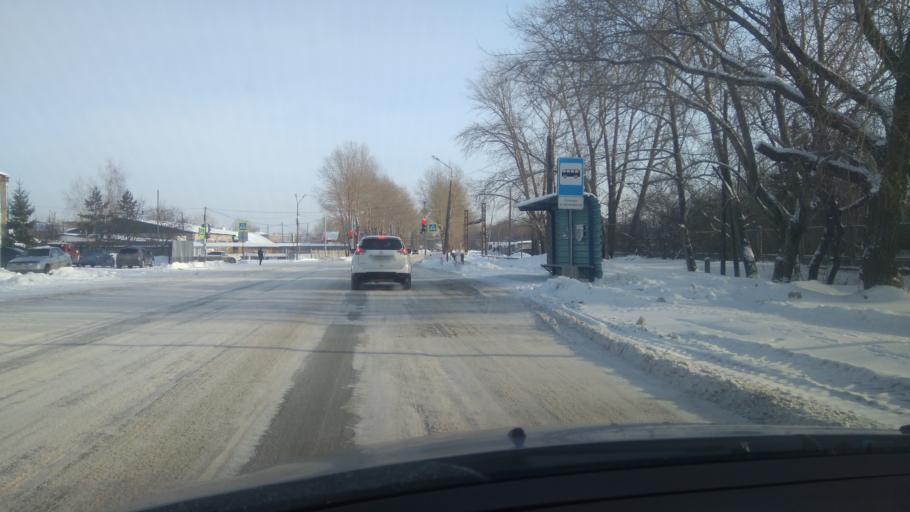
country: RU
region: Sverdlovsk
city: Sukhoy Log
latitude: 56.9109
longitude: 62.0303
